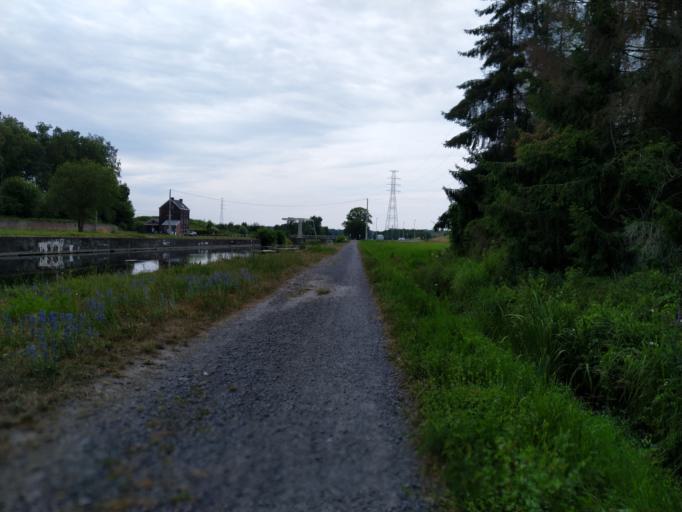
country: BE
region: Wallonia
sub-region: Province du Hainaut
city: Roeulx
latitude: 50.4706
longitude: 4.0711
